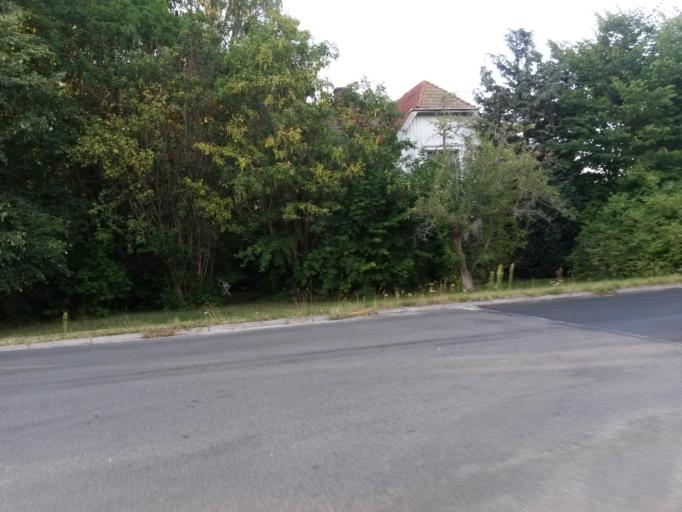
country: SE
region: Vaestra Goetaland
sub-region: Vargarda Kommun
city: Vargarda
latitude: 58.0306
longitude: 12.8052
